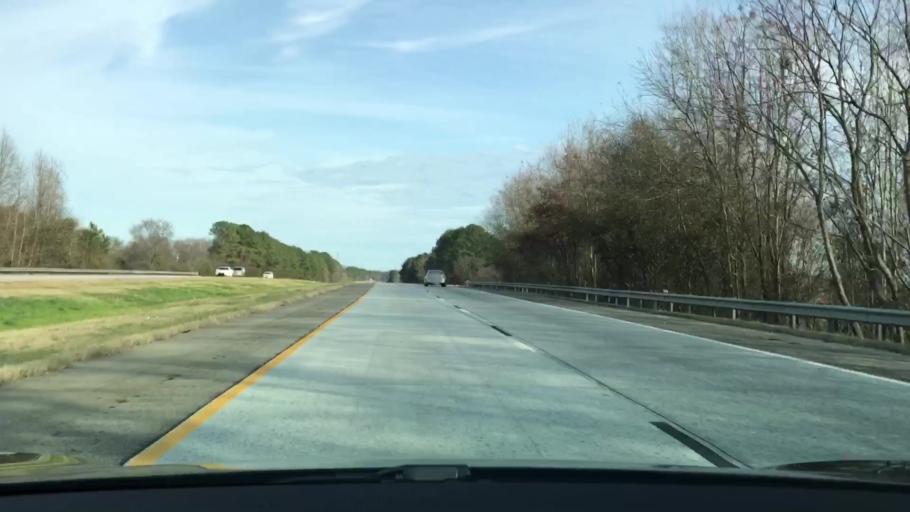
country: US
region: Georgia
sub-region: Morgan County
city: Madison
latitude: 33.5536
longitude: -83.4036
